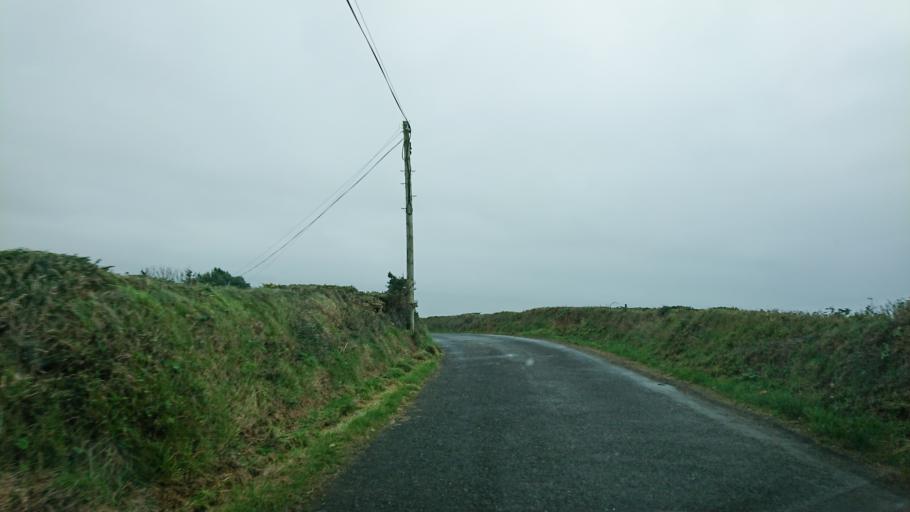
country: IE
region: Munster
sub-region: Waterford
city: Tra Mhor
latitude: 52.1431
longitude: -7.2038
